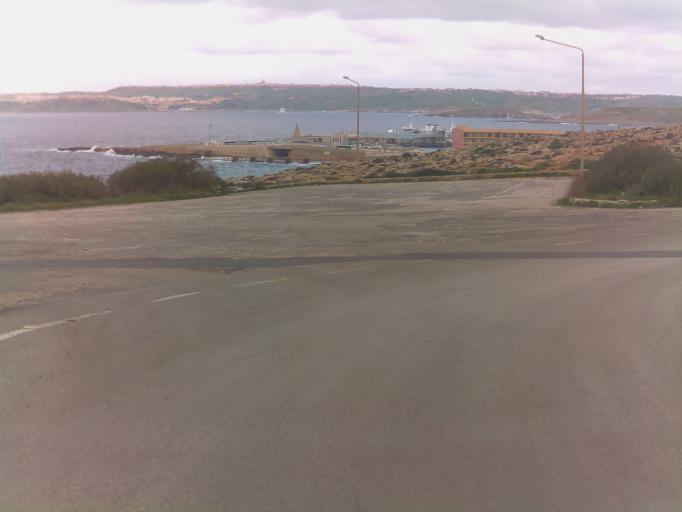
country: MT
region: Il-Mellieha
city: Mellieha
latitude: 35.9807
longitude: 14.3335
